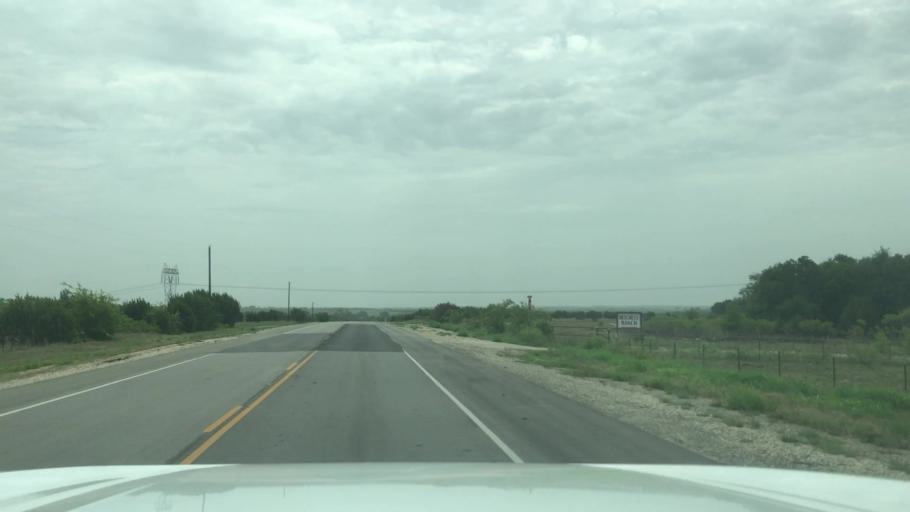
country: US
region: Texas
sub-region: Erath County
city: Dublin
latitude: 32.0776
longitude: -98.2383
